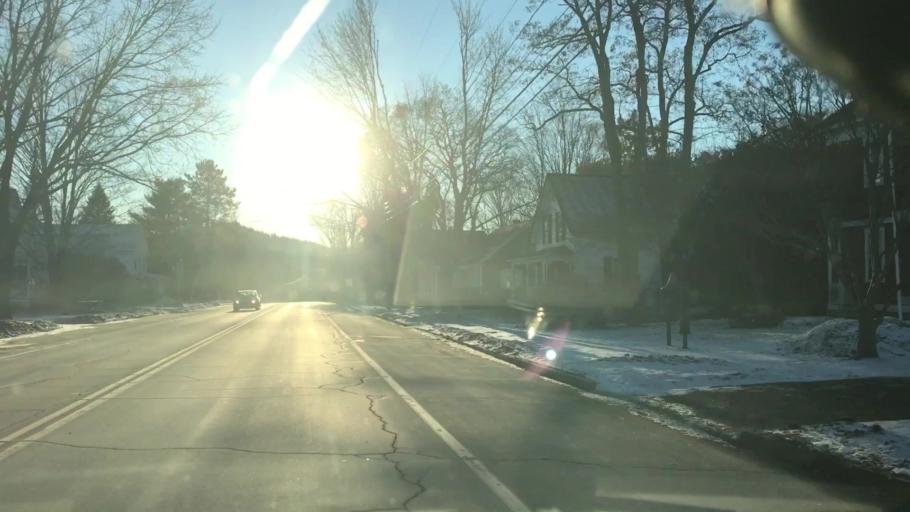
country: US
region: New Hampshire
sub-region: Grafton County
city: Lyme
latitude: 43.8100
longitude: -72.1601
